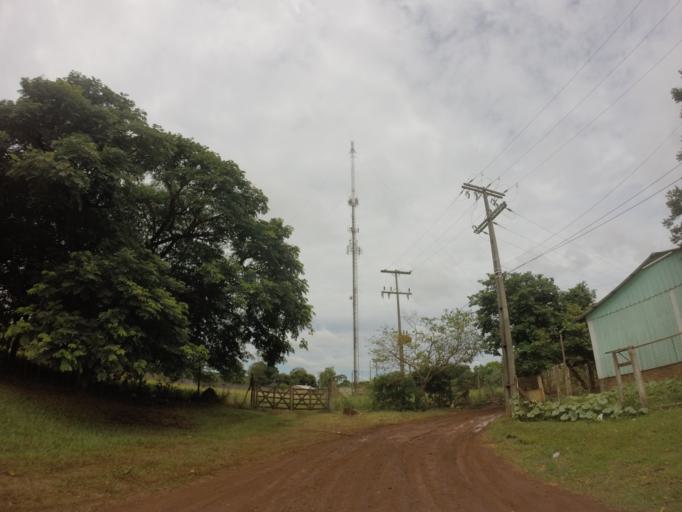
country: PY
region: Alto Parana
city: Ciudad del Este
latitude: -25.4032
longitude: -54.6320
